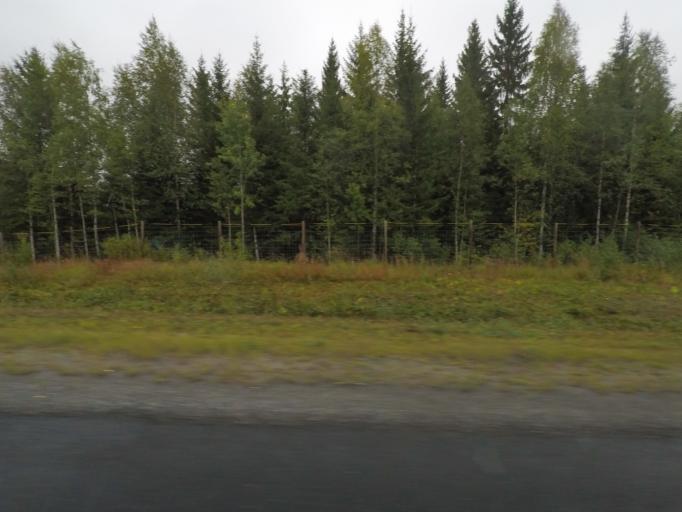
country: FI
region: Northern Savo
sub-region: Kuopio
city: Kuopio
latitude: 62.7877
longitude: 27.5940
